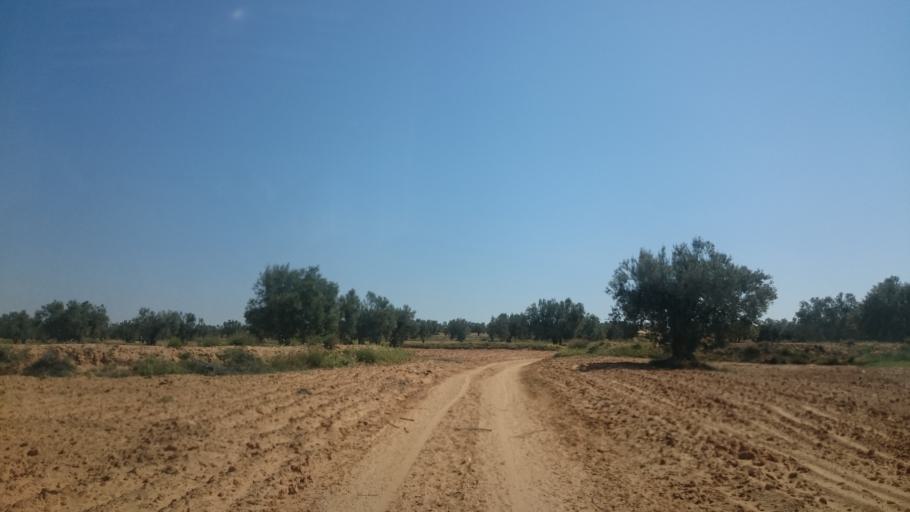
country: TN
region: Safaqis
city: Sfax
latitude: 34.7930
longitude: 10.5491
